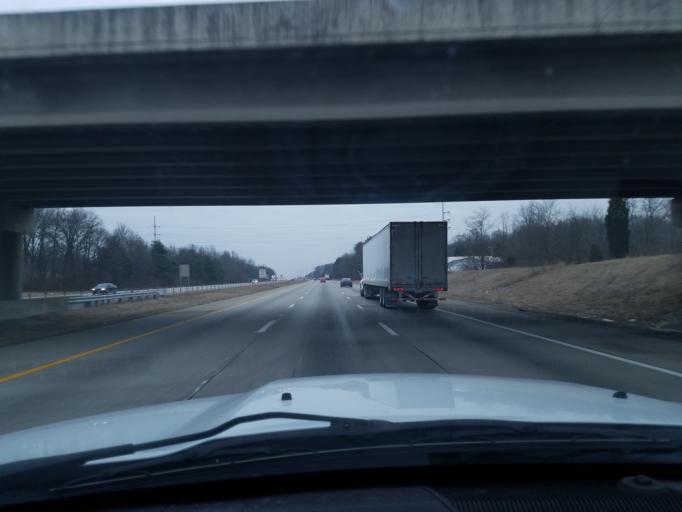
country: US
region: Kentucky
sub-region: Bullitt County
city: Hillview
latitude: 38.0915
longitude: -85.7012
